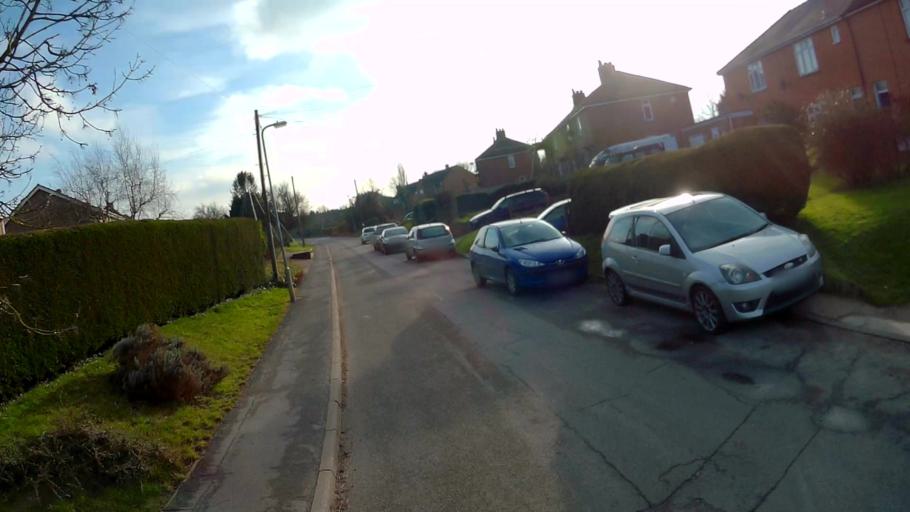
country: GB
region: England
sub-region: Lincolnshire
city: Bourne
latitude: 52.7410
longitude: -0.3828
